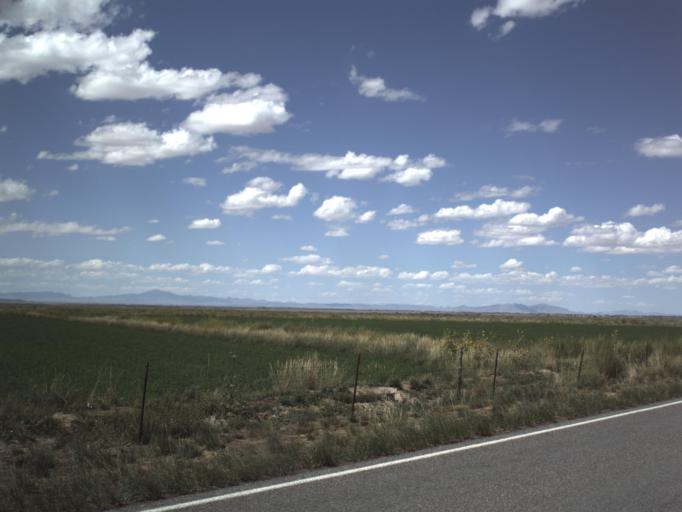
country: US
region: Utah
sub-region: Millard County
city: Delta
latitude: 39.2130
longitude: -112.4158
